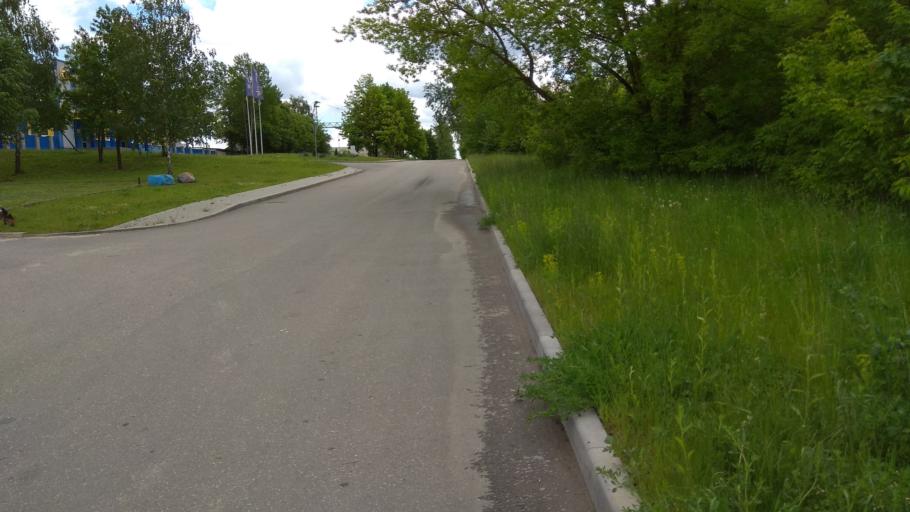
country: BY
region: Grodnenskaya
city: Hrodna
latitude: 53.7138
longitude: 23.7980
